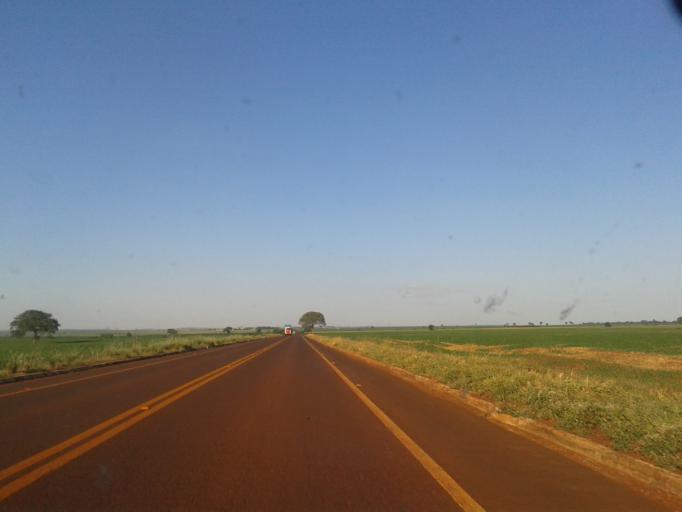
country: BR
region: Minas Gerais
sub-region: Capinopolis
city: Capinopolis
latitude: -18.7115
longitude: -49.7270
